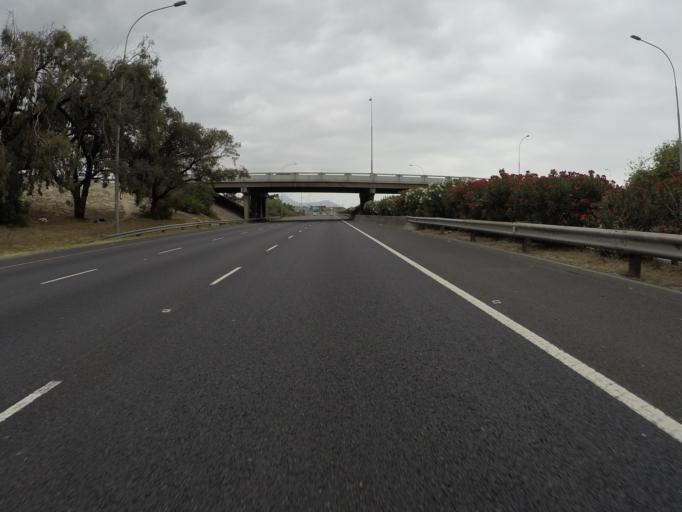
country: ZA
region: Western Cape
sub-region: City of Cape Town
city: Sunset Beach
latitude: -33.8904
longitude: 18.5542
